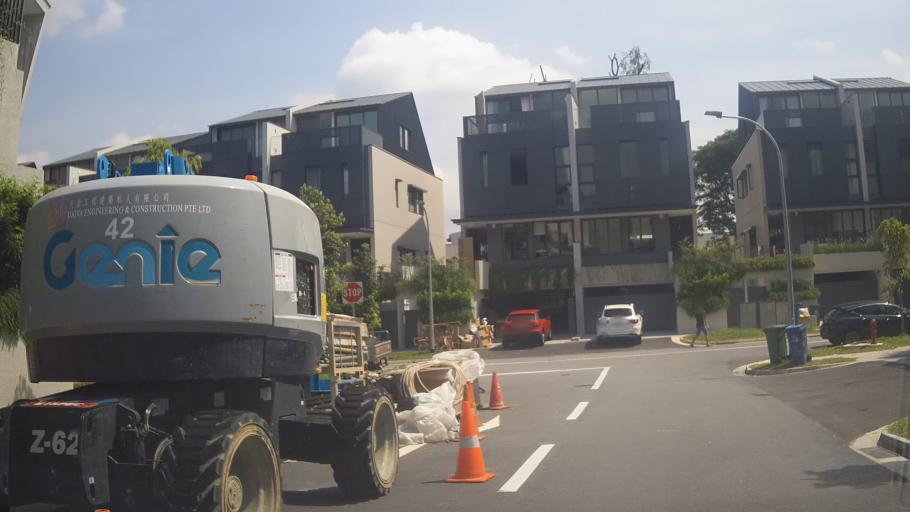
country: SG
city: Singapore
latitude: 1.3220
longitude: 103.8037
